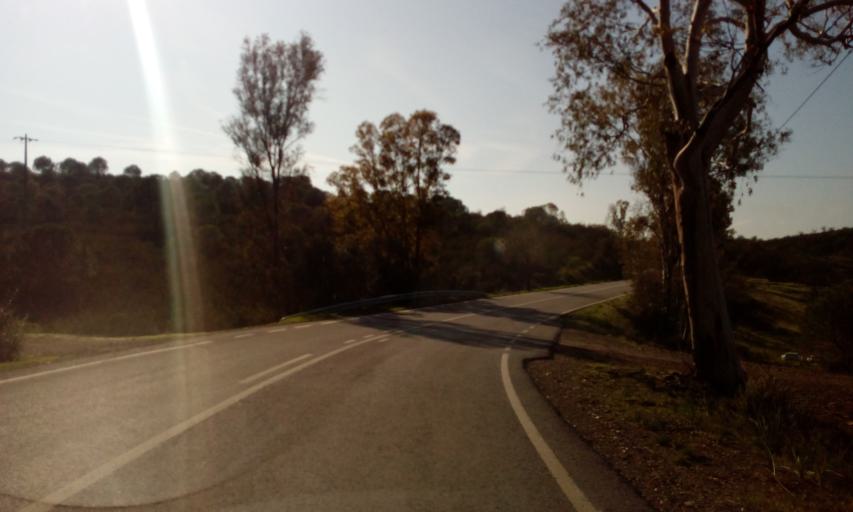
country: PT
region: Faro
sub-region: Alcoutim
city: Alcoutim
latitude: 37.4584
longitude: -7.4823
